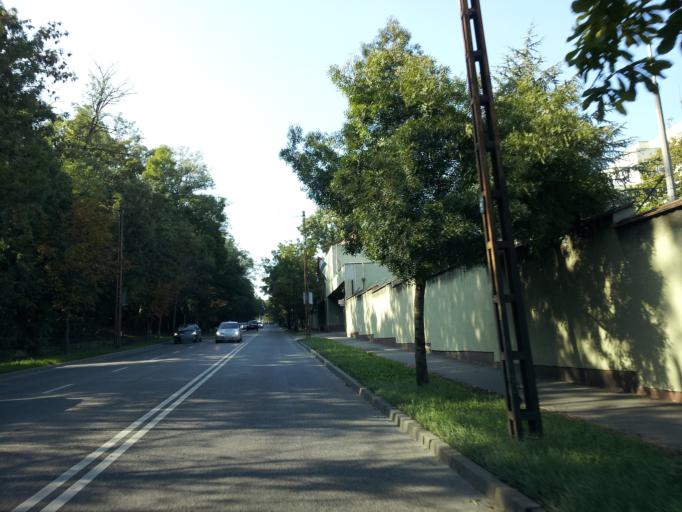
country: HU
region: Pest
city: Budakeszi
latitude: 47.5317
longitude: 18.9775
